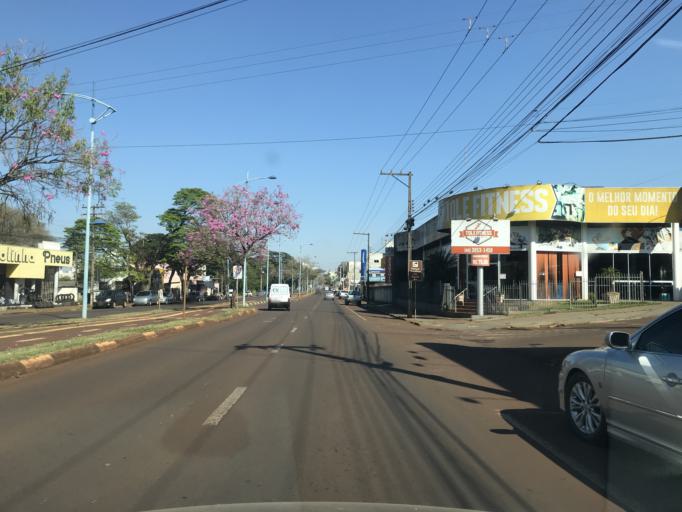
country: BR
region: Parana
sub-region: Toledo
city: Toledo
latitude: -24.7256
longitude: -53.7282
